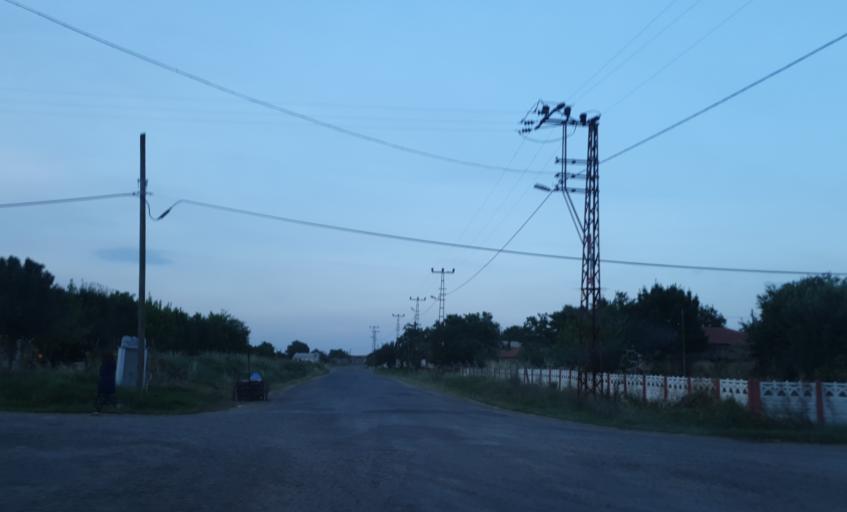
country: TR
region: Tekirdag
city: Beyazkoy
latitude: 41.4395
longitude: 27.6992
